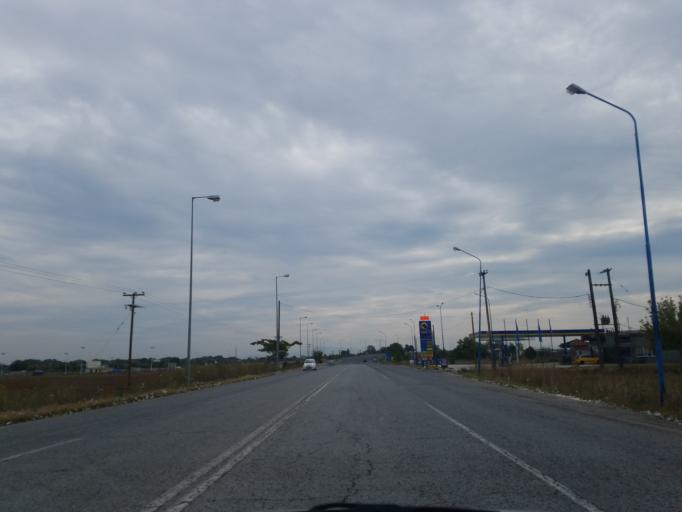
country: GR
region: Thessaly
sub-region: Nomos Kardhitsas
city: Sofades
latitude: 39.3452
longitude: 22.0770
